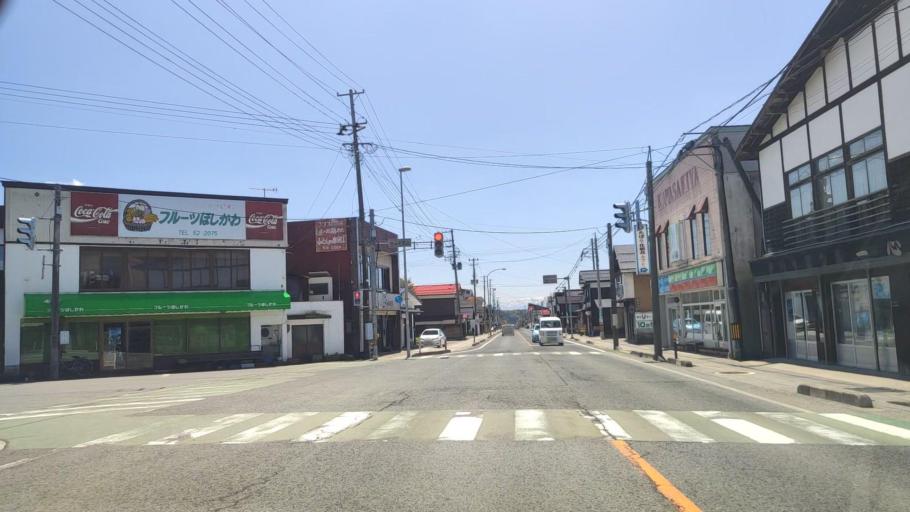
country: JP
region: Yamagata
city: Shinjo
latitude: 38.8824
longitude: 140.3368
